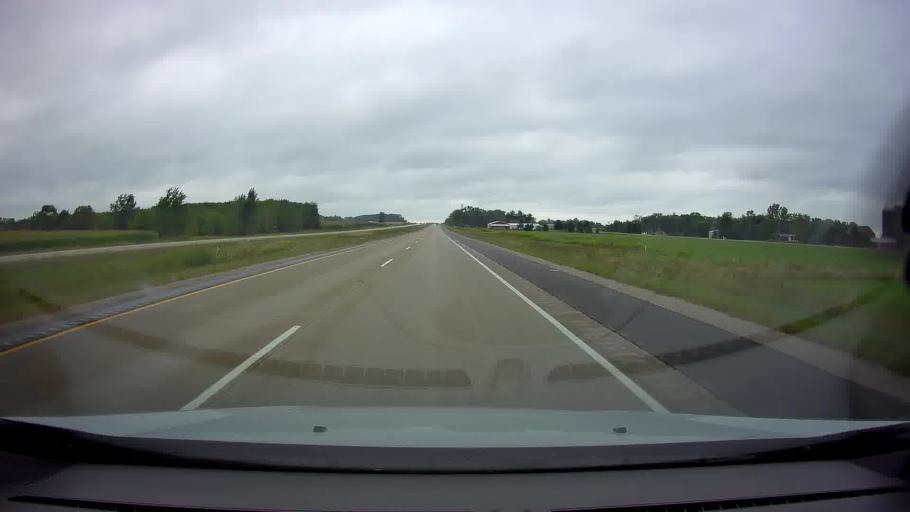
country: US
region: Wisconsin
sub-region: Brown County
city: Pulaski
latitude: 44.6358
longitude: -88.2844
